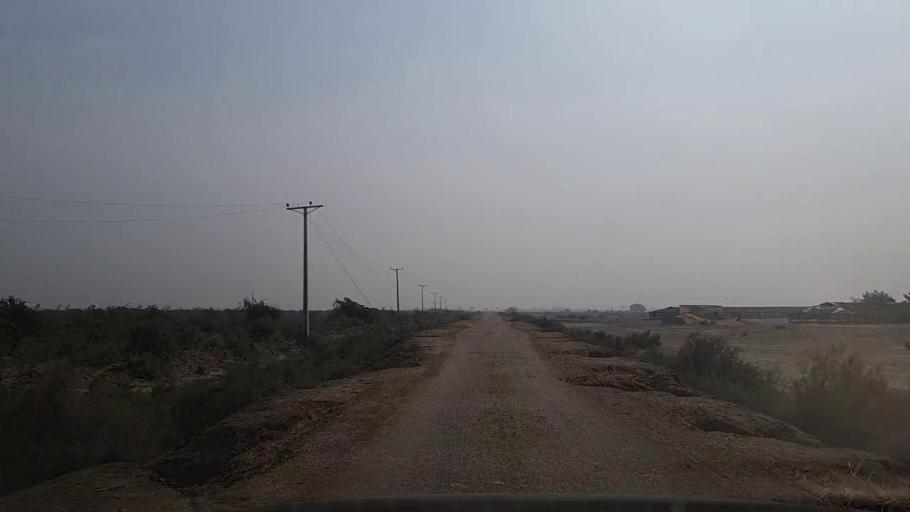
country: PK
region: Sindh
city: Mirpur Sakro
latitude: 24.3900
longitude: 67.7519
